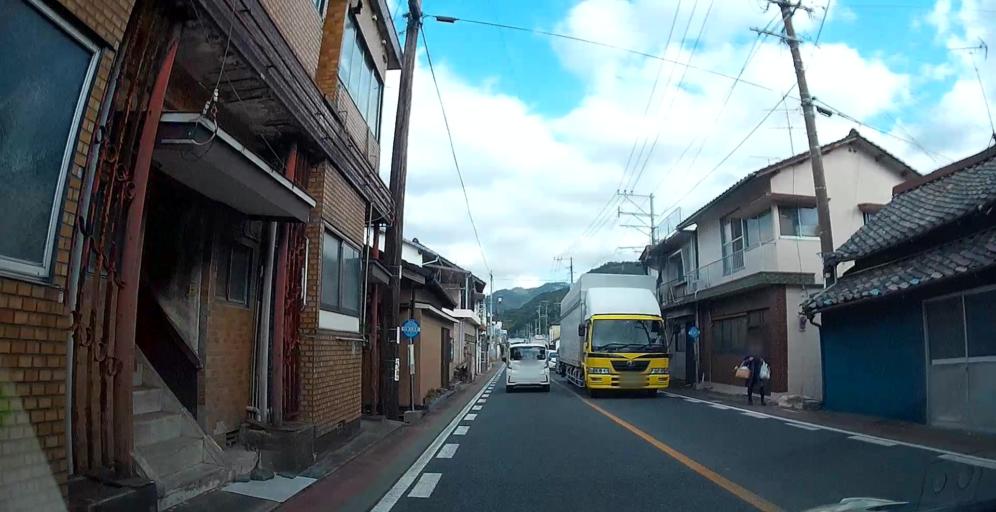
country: JP
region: Kumamoto
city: Yatsushiro
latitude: 32.4342
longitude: 130.5756
